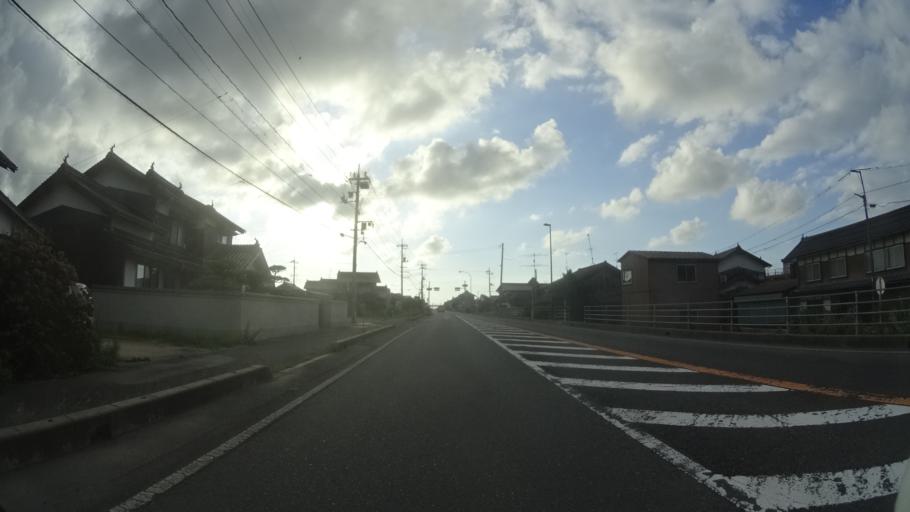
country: JP
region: Tottori
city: Kurayoshi
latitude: 35.5236
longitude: 133.5921
